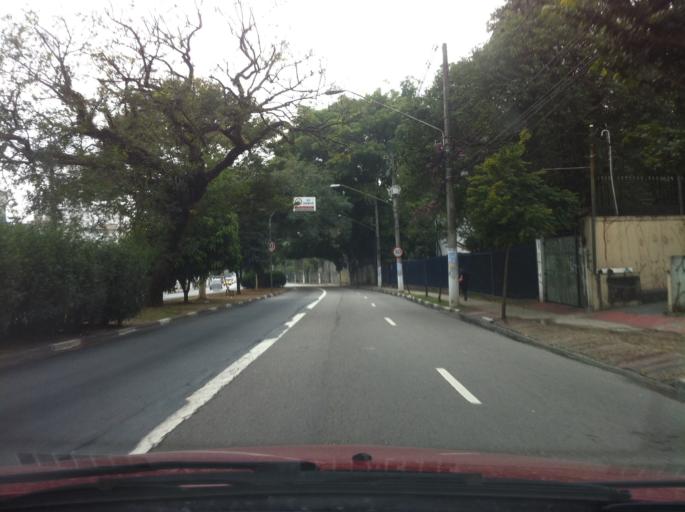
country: BR
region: Sao Paulo
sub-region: Diadema
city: Diadema
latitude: -23.6315
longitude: -46.6911
